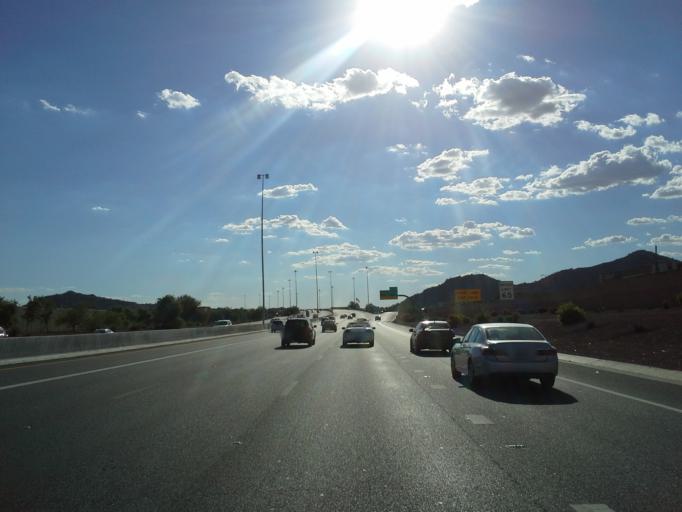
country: US
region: Arizona
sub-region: Maricopa County
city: Paradise Valley
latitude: 33.6729
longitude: -112.0228
